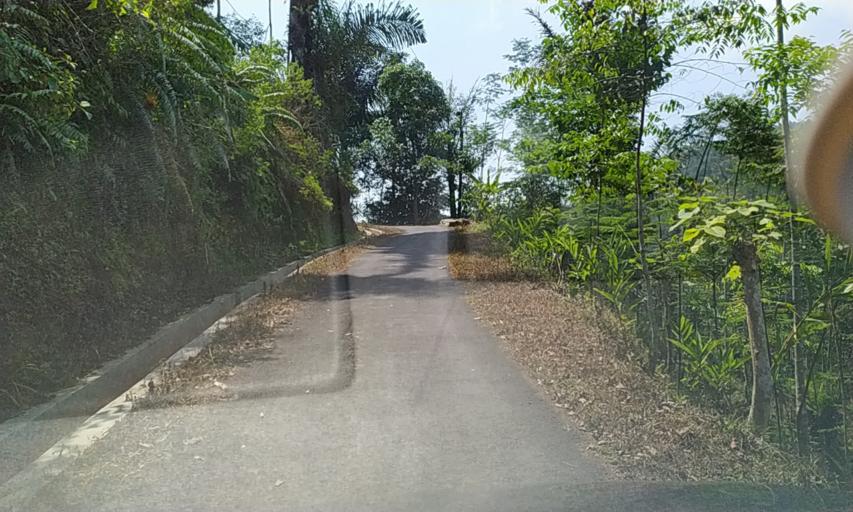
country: ID
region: Central Java
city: Kaduluhur
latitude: -7.1841
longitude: 108.6313
